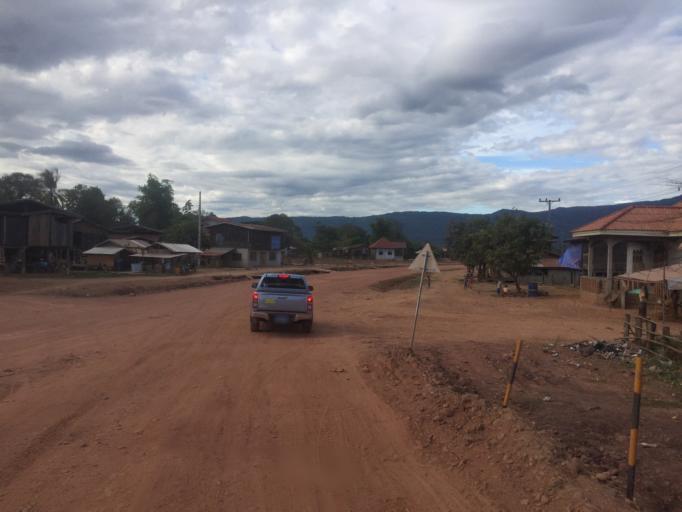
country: LA
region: Attapu
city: Attapu
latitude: 14.6959
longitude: 106.5325
